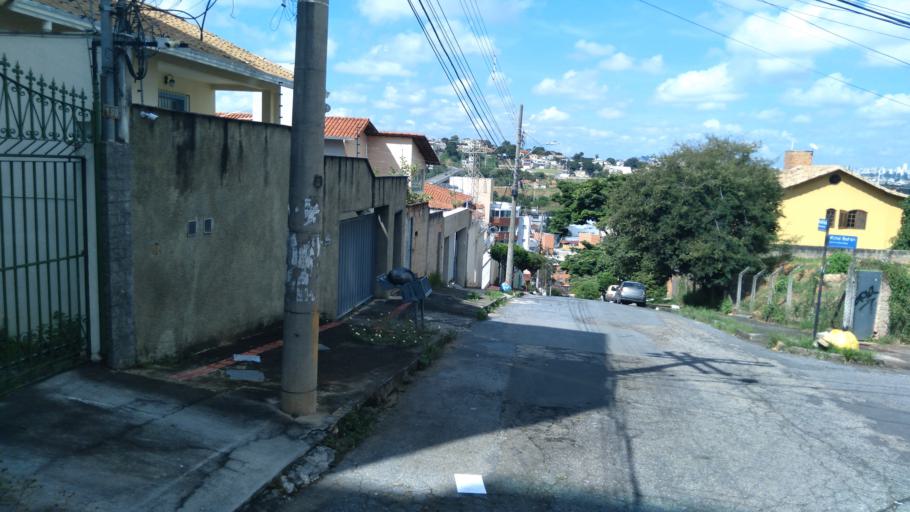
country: BR
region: Minas Gerais
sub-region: Belo Horizonte
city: Belo Horizonte
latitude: -19.8723
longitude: -43.9178
